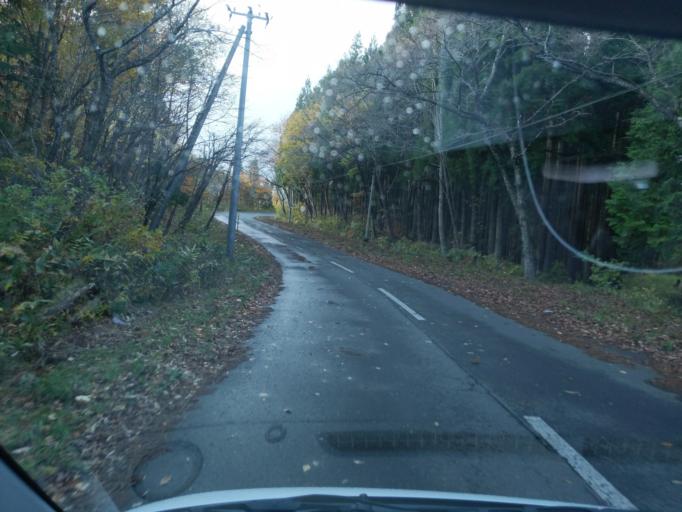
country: JP
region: Iwate
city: Mizusawa
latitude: 39.0303
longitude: 141.0892
